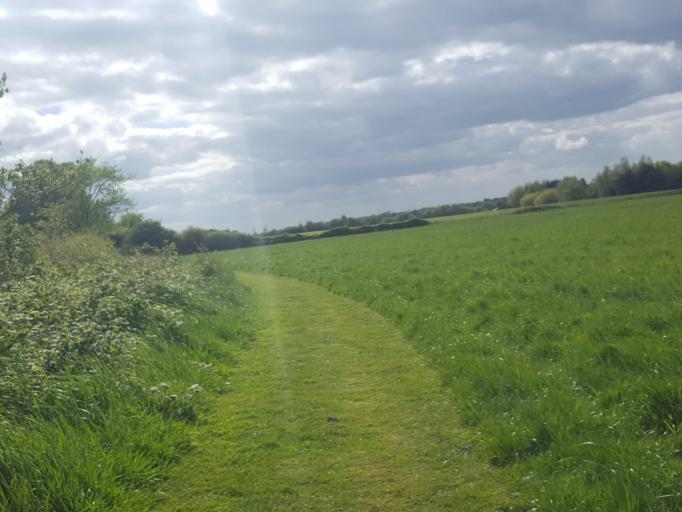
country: GB
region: England
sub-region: Essex
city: Frinton-on-Sea
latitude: 51.8324
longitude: 1.2062
